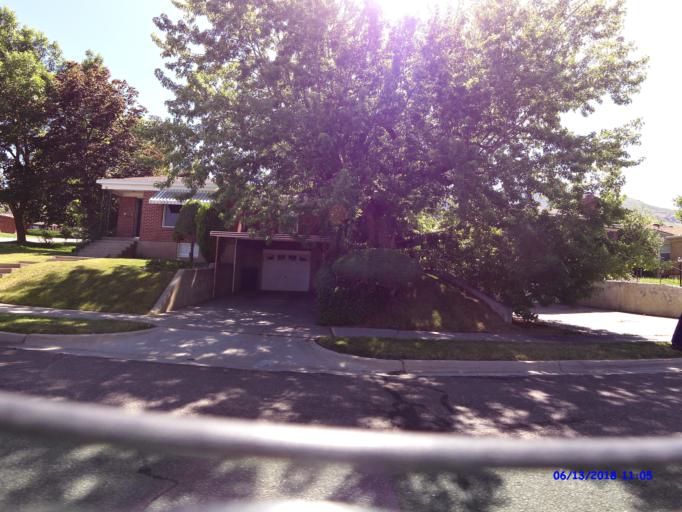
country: US
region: Utah
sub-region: Weber County
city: South Ogden
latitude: 41.2097
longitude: -111.9442
